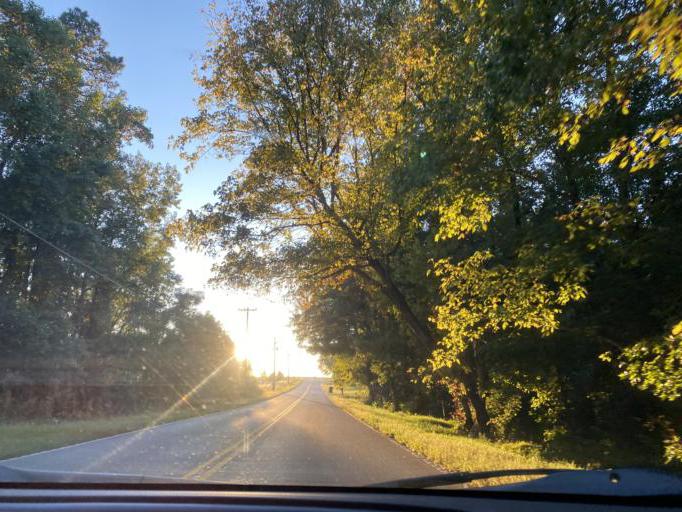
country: US
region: South Carolina
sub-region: Cherokee County
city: Gaffney
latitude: 35.0973
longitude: -81.6606
